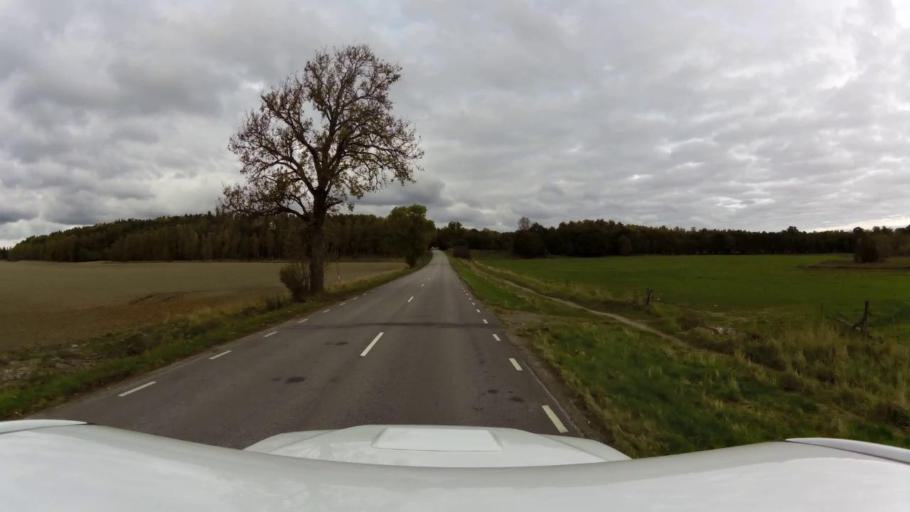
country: SE
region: OEstergoetland
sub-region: Linkopings Kommun
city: Berg
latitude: 58.5048
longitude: 15.5396
